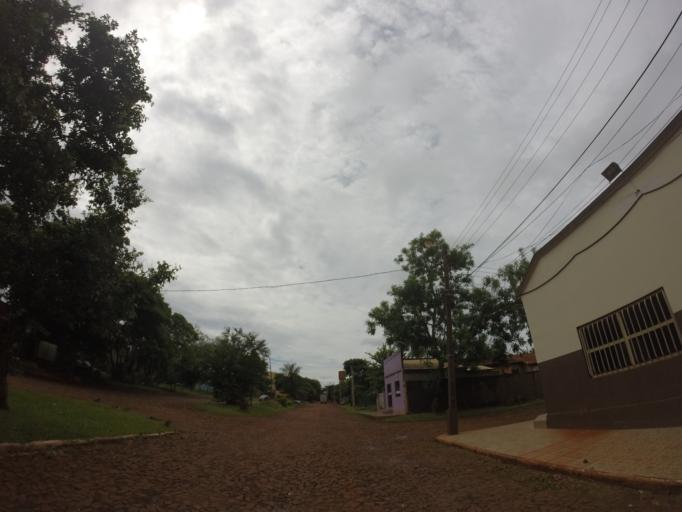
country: PY
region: Alto Parana
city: Ciudad del Este
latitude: -25.3834
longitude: -54.6582
